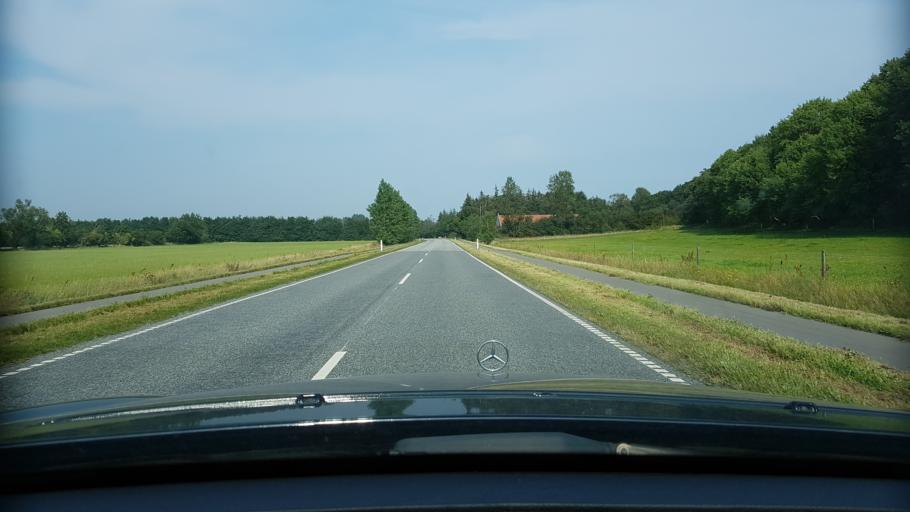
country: DK
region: North Denmark
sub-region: Alborg Kommune
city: Hals
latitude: 56.9174
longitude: 10.2581
